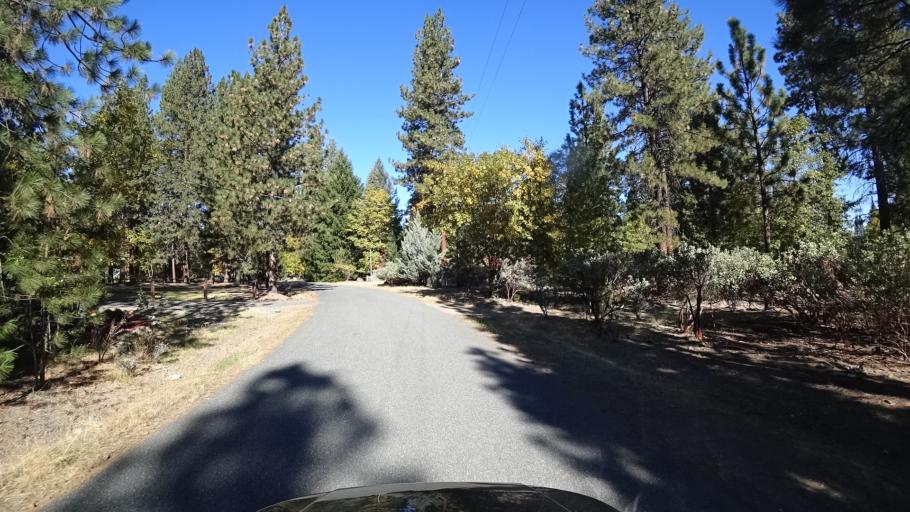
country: US
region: California
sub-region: Siskiyou County
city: Yreka
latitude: 41.5218
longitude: -122.9193
